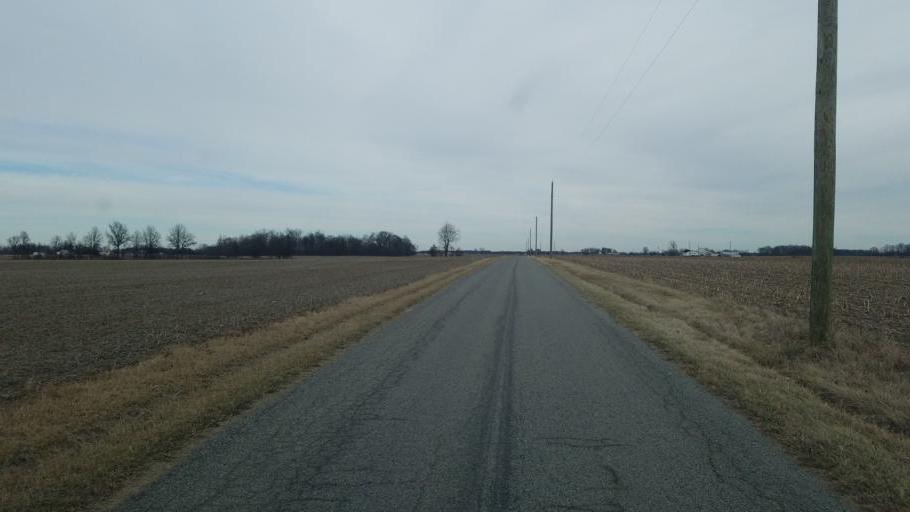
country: US
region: Ohio
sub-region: Union County
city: Richwood
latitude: 40.4950
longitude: -83.3765
